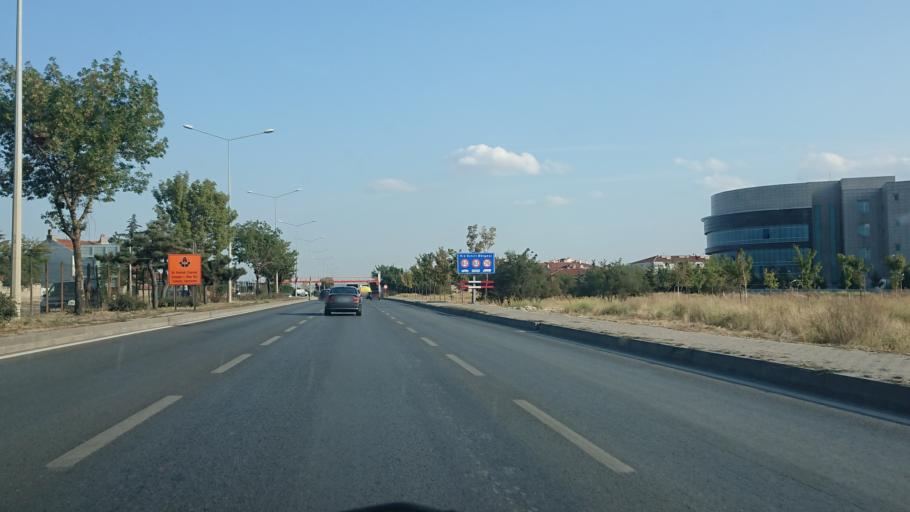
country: TR
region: Eskisehir
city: Eskisehir
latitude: 39.7693
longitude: 30.5617
